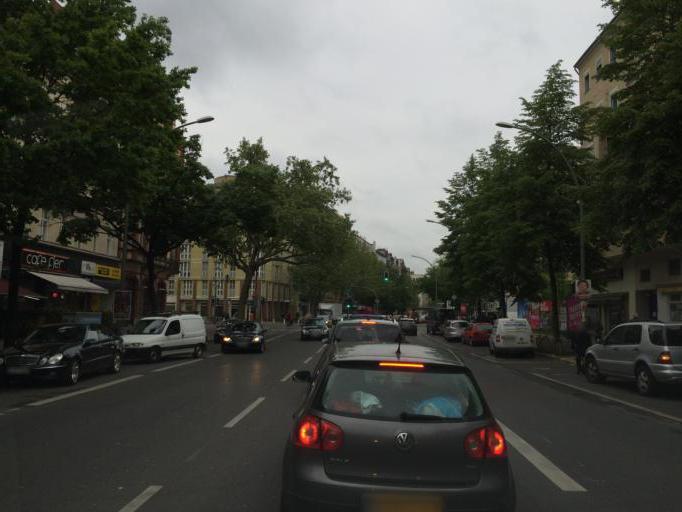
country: DE
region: Berlin
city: Berlin Schoeneberg
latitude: 52.4953
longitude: 13.3612
